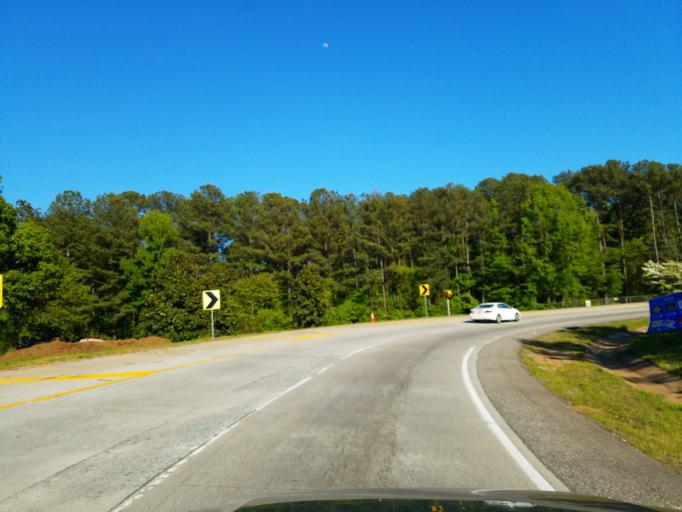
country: US
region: Georgia
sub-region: Fulton County
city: Roswell
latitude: 34.0230
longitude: -84.3225
